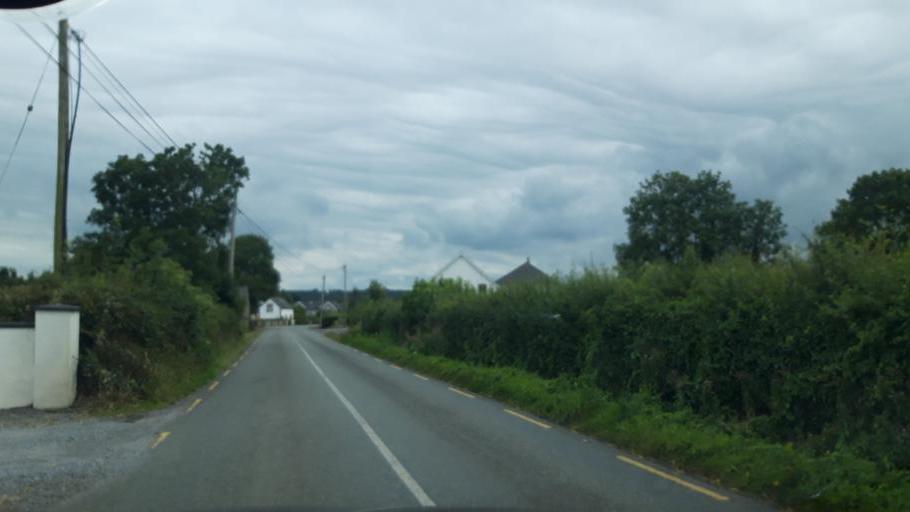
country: IE
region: Leinster
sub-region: Kilkenny
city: Ballyragget
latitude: 52.7404
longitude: -7.3984
